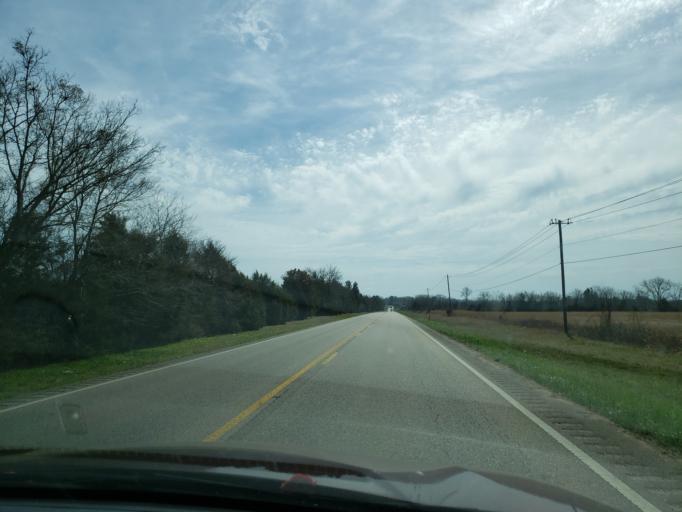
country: US
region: Alabama
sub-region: Dallas County
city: Selma
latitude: 32.4427
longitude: -87.0695
